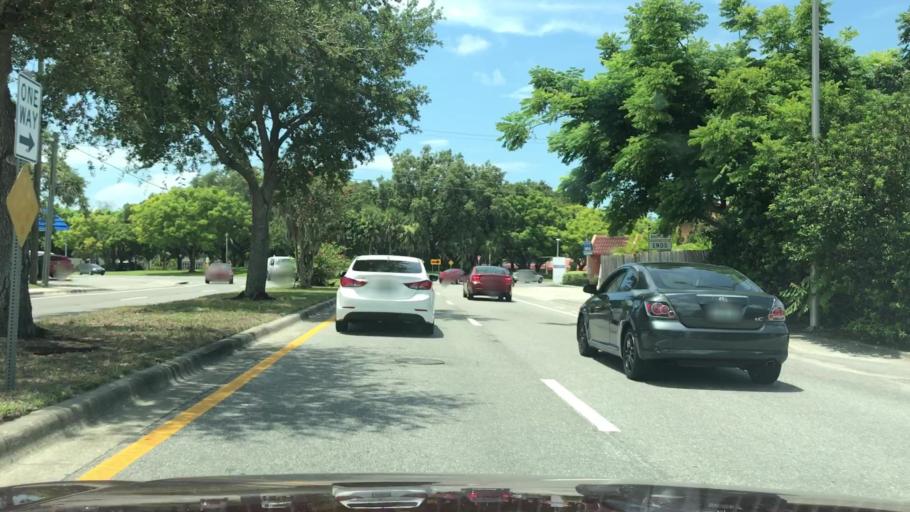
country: US
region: Florida
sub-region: Sarasota County
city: Southgate
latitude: 27.3068
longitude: -82.5142
